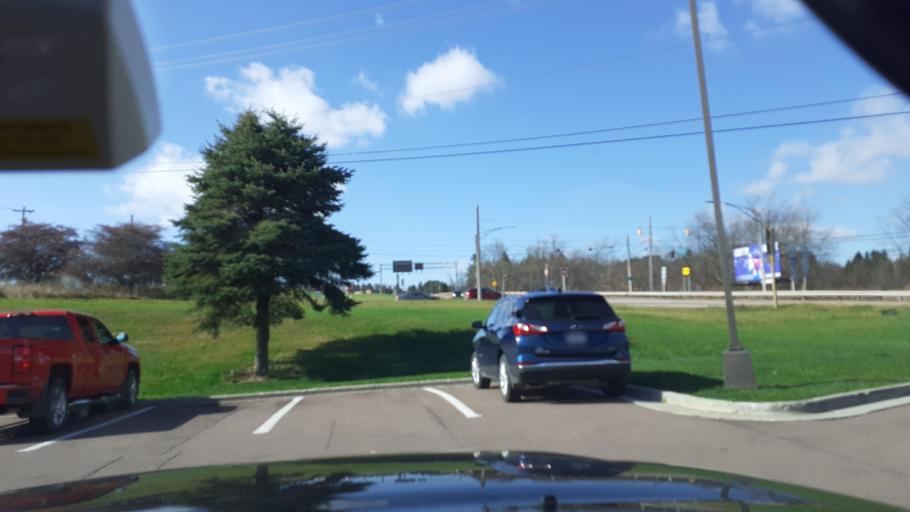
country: US
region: Pennsylvania
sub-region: Somerset County
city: Meyersdale
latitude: 39.6943
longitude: -79.2471
